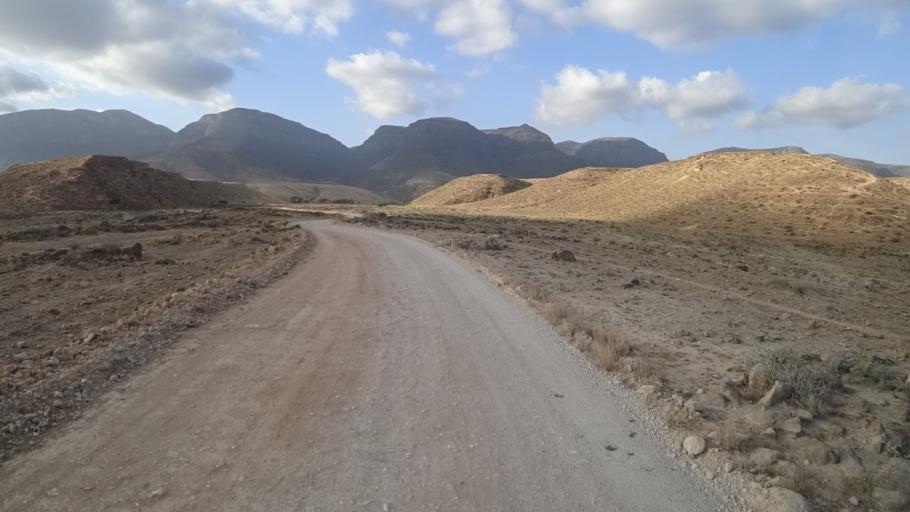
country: OM
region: Zufar
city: Salalah
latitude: 16.9799
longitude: 53.8528
